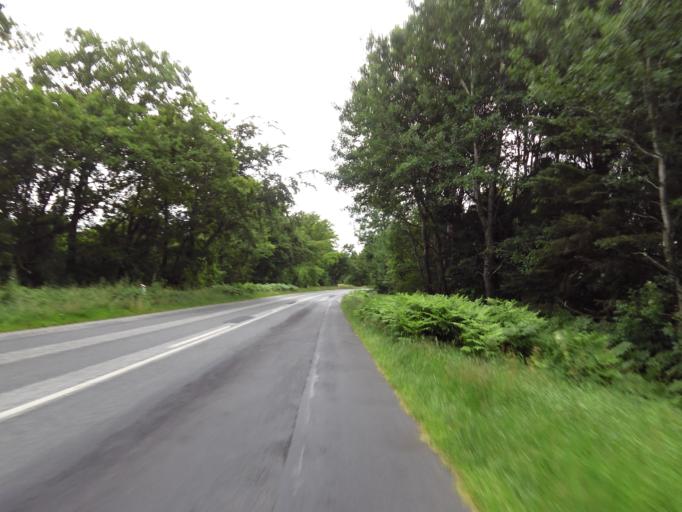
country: DK
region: South Denmark
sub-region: Tonder Kommune
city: Toftlund
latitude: 55.1850
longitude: 8.9598
